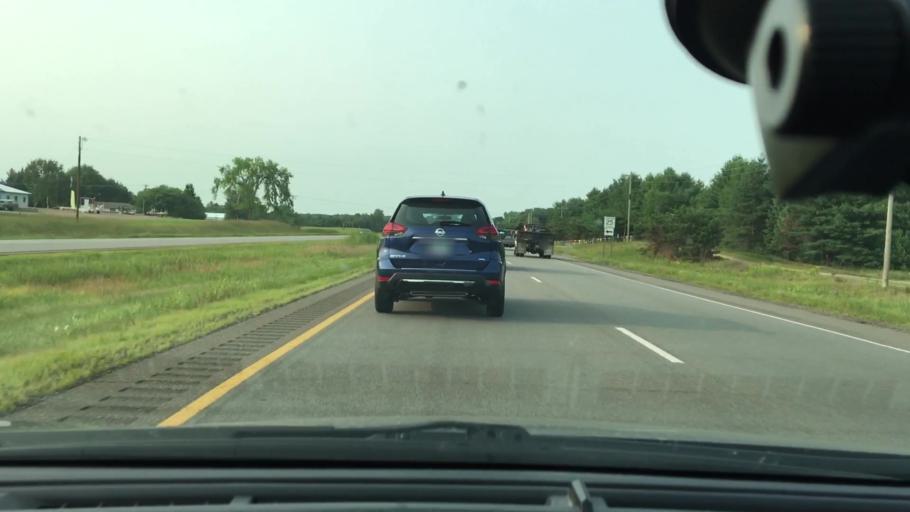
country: US
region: Minnesota
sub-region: Sherburne County
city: Zimmerman
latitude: 45.4087
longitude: -93.5656
